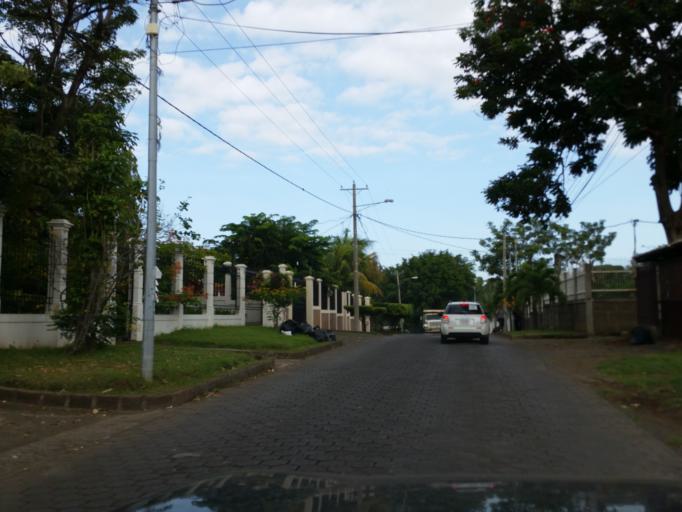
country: NI
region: Managua
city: Managua
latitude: 12.0999
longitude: -86.2358
